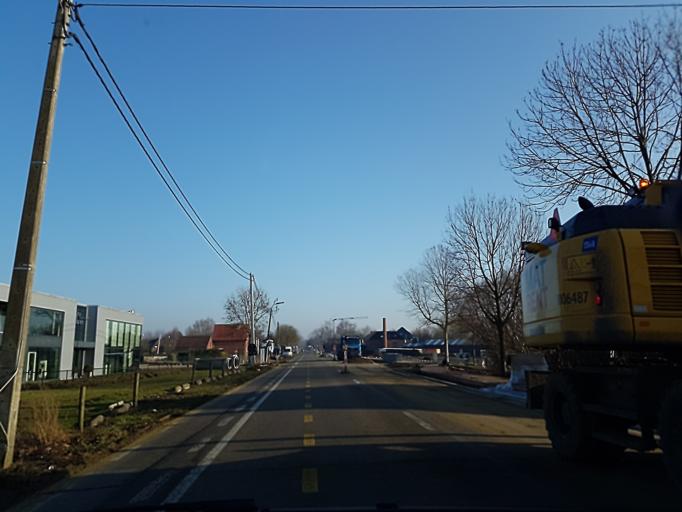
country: BE
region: Flanders
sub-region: Provincie Vlaams-Brabant
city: Tremelo
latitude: 50.9700
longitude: 4.6850
